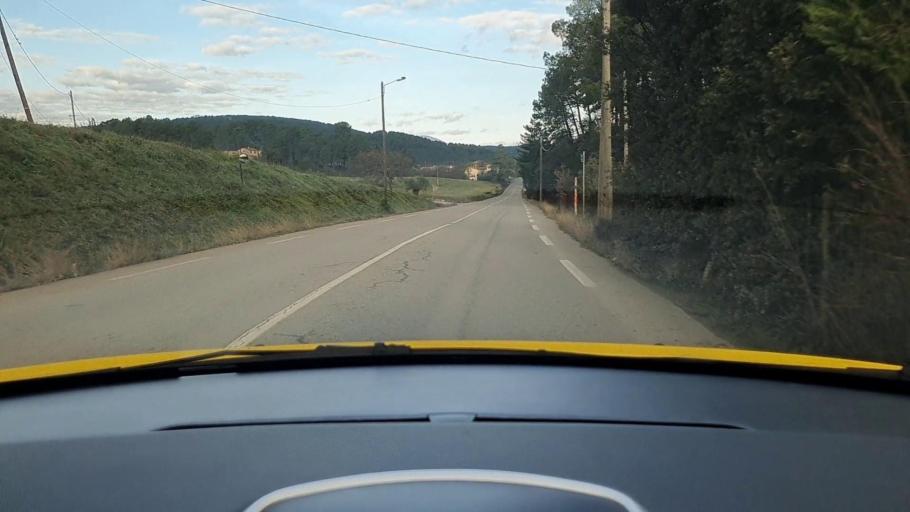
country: FR
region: Languedoc-Roussillon
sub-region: Departement du Gard
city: Laval-Pradel
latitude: 44.2255
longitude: 4.0645
